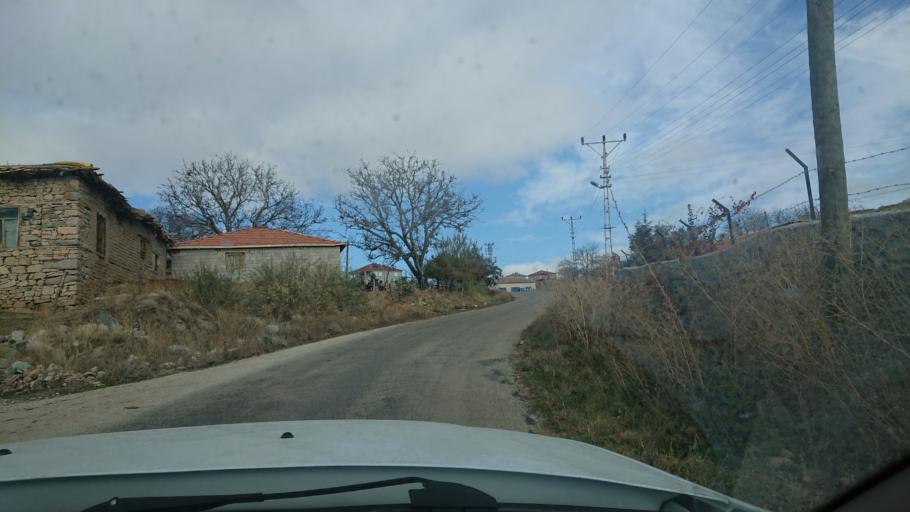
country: TR
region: Aksaray
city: Agacoren
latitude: 38.8221
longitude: 33.9585
